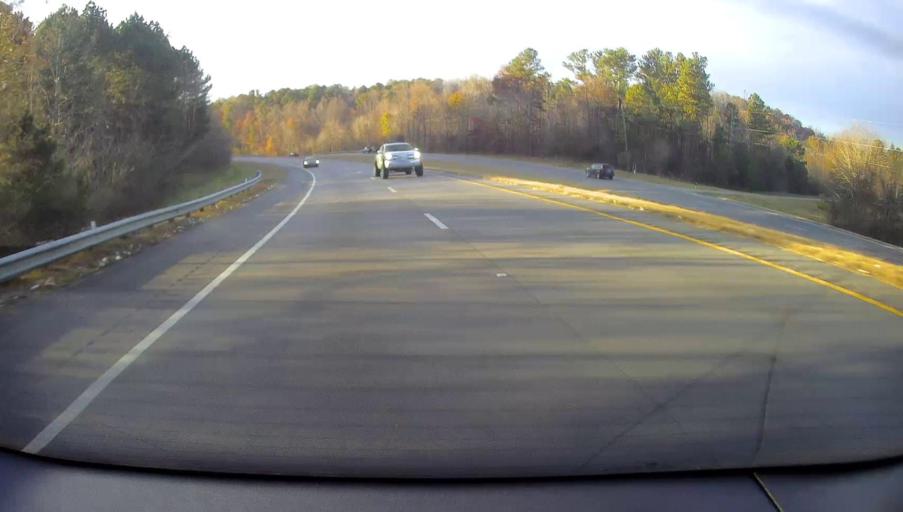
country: US
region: Alabama
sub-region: Blount County
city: Blountsville
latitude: 34.1620
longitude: -86.5007
